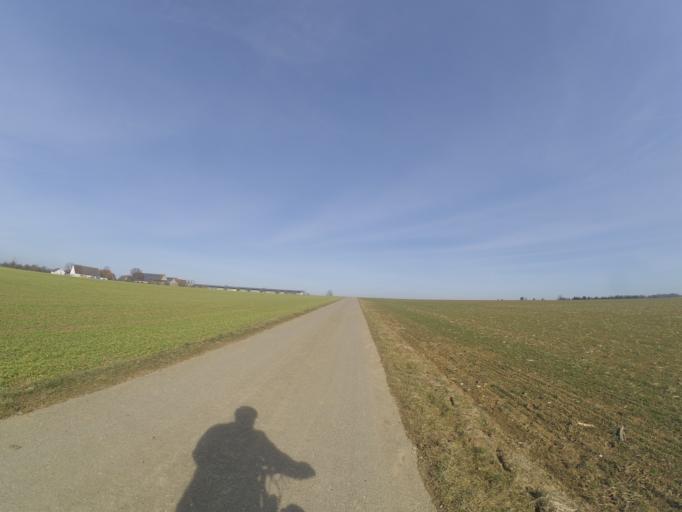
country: DE
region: Baden-Wuerttemberg
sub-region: Tuebingen Region
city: Beimerstetten
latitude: 48.4672
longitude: 9.9965
